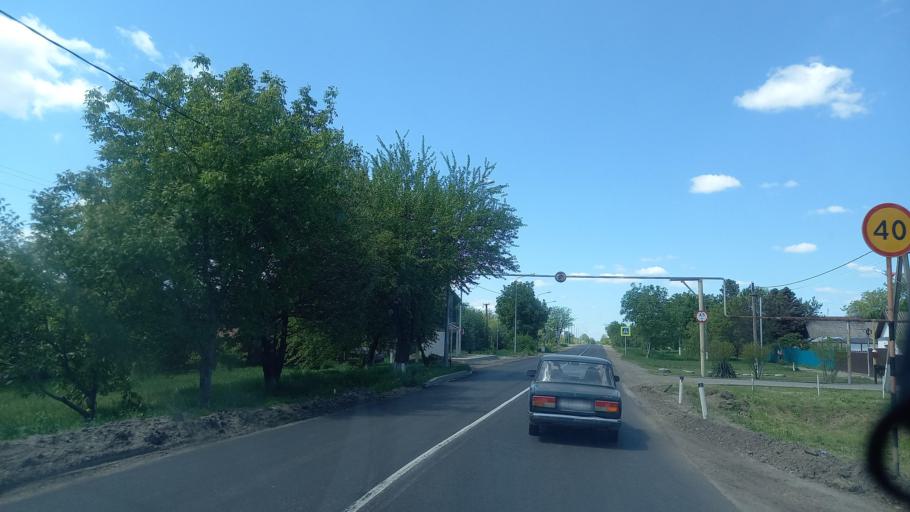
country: RU
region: Krasnodarskiy
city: Tbilisskaya
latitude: 45.3252
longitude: 40.2414
